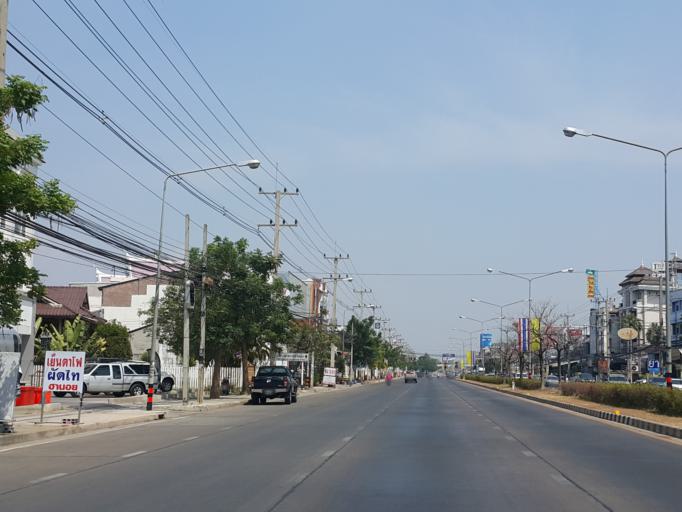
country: TH
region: Phitsanulok
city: Phitsanulok
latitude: 16.8282
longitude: 100.2531
